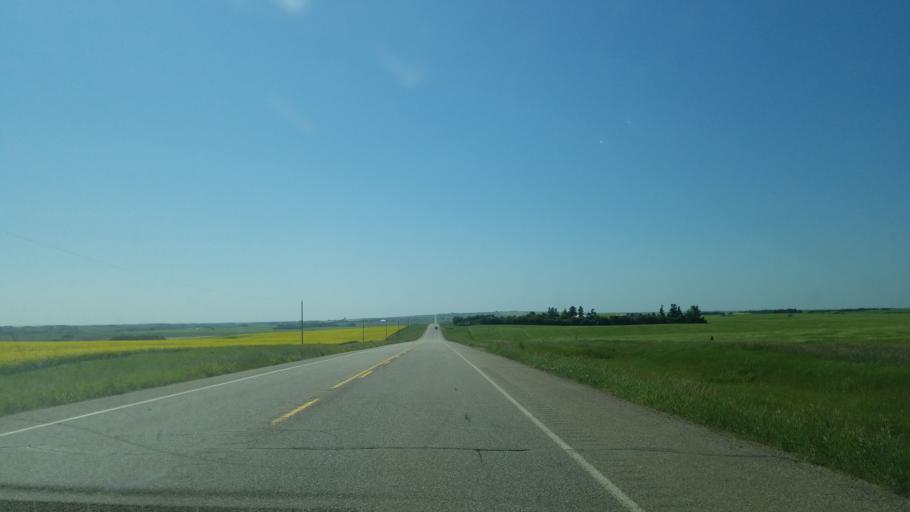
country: CA
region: Saskatchewan
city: Macklin
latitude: 52.3613
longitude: -110.0304
